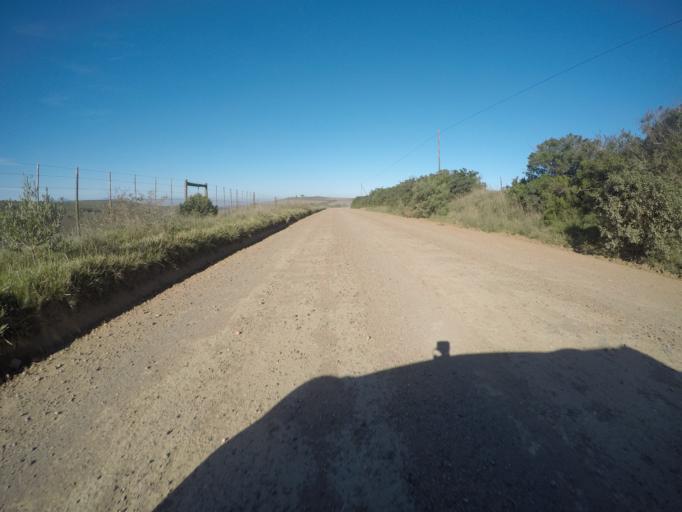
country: ZA
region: Western Cape
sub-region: Eden District Municipality
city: Mossel Bay
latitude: -34.1444
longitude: 22.0053
